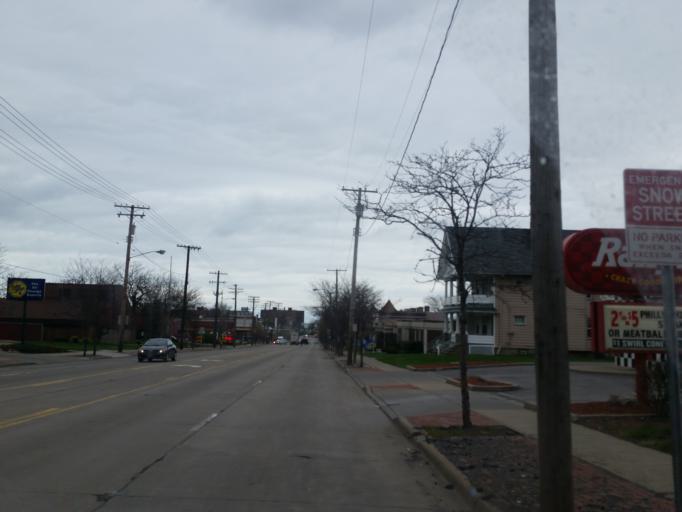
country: US
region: Ohio
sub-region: Cuyahoga County
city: Lakewood
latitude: 41.4810
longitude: -81.7686
